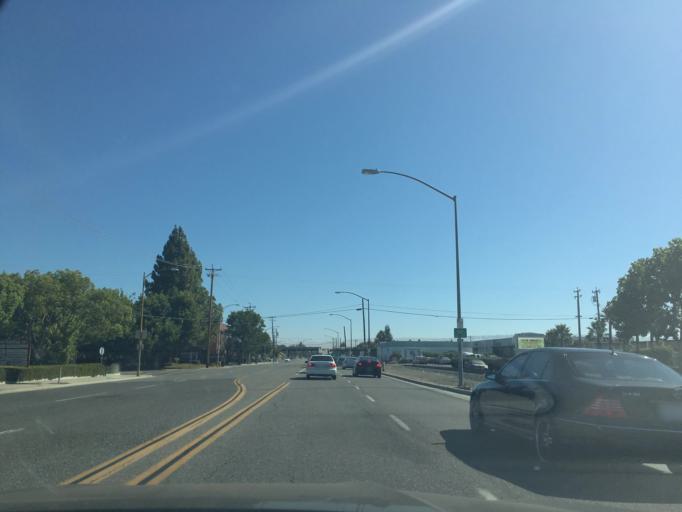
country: US
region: California
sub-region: Santa Clara County
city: Campbell
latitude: 37.2695
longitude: -121.9559
